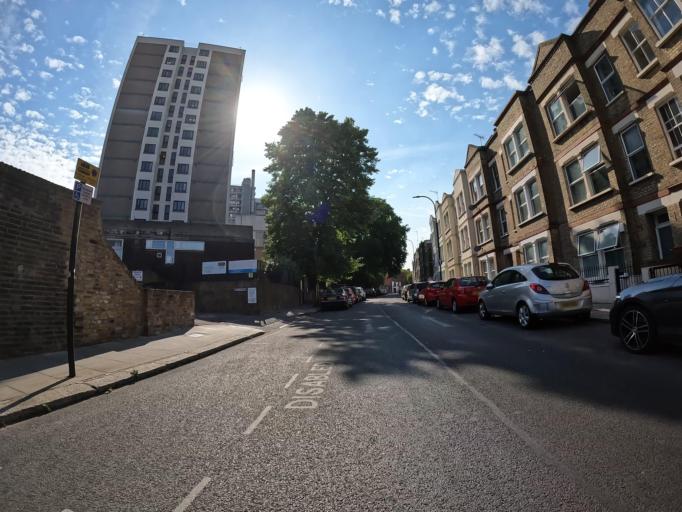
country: GB
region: England
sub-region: Greater London
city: Hendon
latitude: 51.5885
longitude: -0.2212
